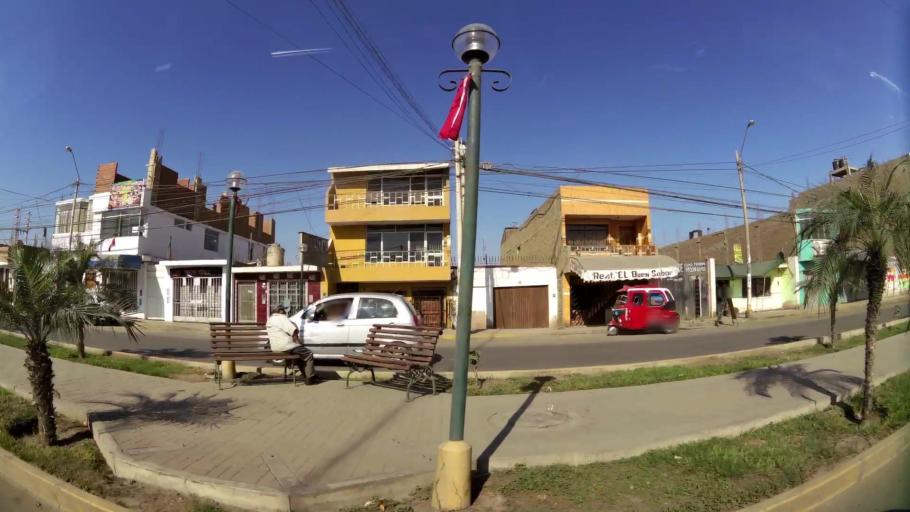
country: PE
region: Ica
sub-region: Provincia de Chincha
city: Chincha Alta
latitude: -13.4063
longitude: -76.1302
